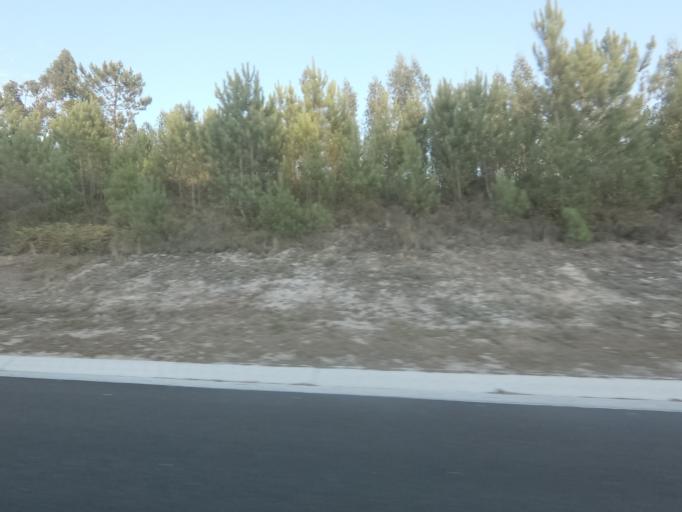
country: PT
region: Leiria
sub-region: Leiria
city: Caranguejeira
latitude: 39.7809
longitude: -8.7379
